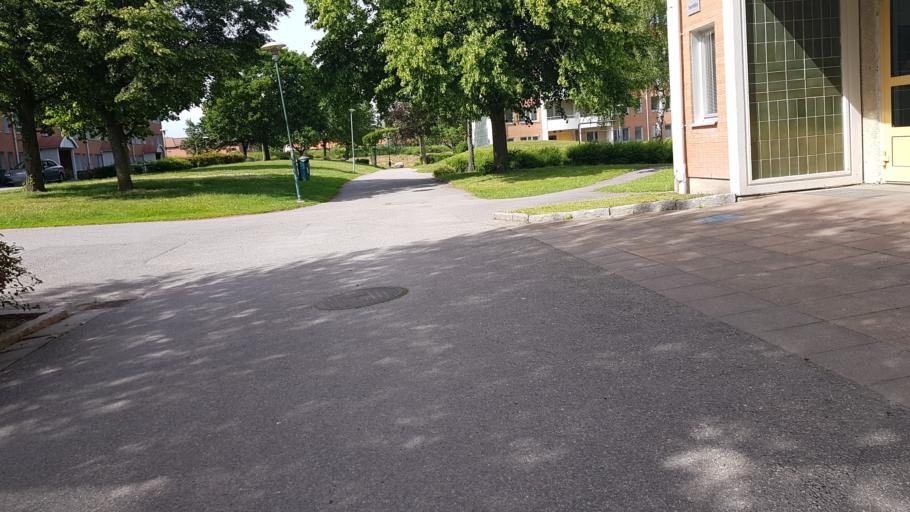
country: SE
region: OEstergoetland
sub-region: Norrkopings Kommun
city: Norrkoping
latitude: 58.5773
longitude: 16.2075
